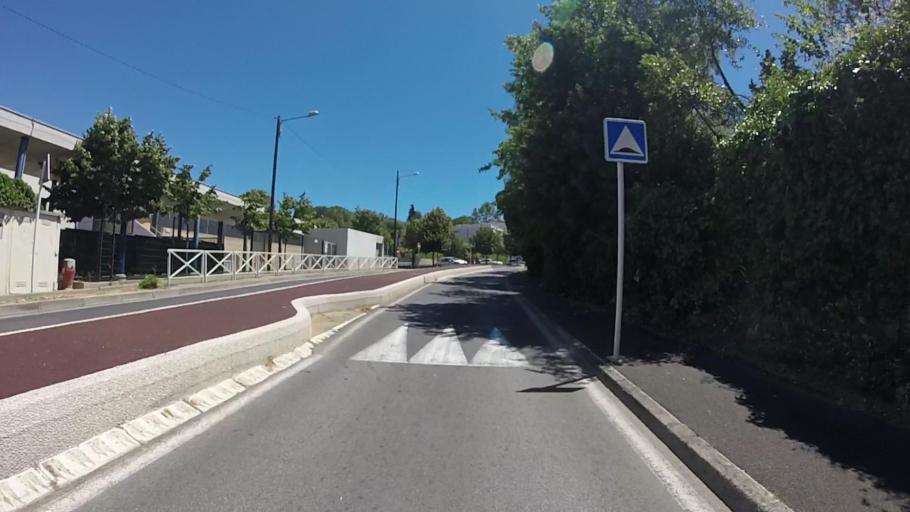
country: FR
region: Provence-Alpes-Cote d'Azur
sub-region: Departement des Alpes-Maritimes
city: Antibes
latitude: 43.5847
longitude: 7.1027
